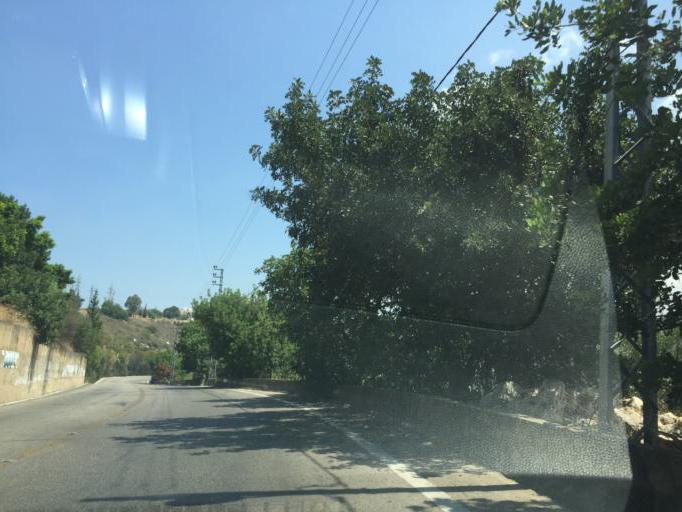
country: LB
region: Mont-Liban
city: Beit ed Dine
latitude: 33.7057
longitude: 35.4521
